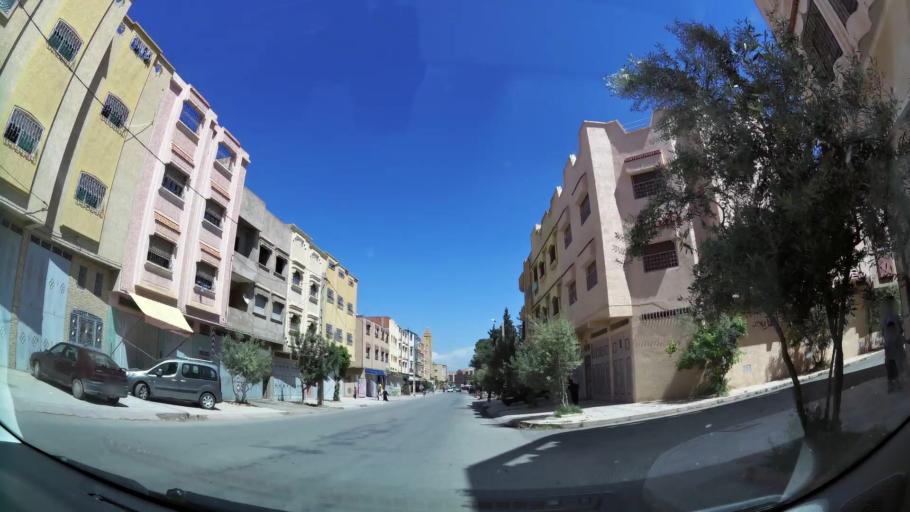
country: MA
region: Oriental
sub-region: Oujda-Angad
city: Oujda
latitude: 34.6870
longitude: -1.9395
